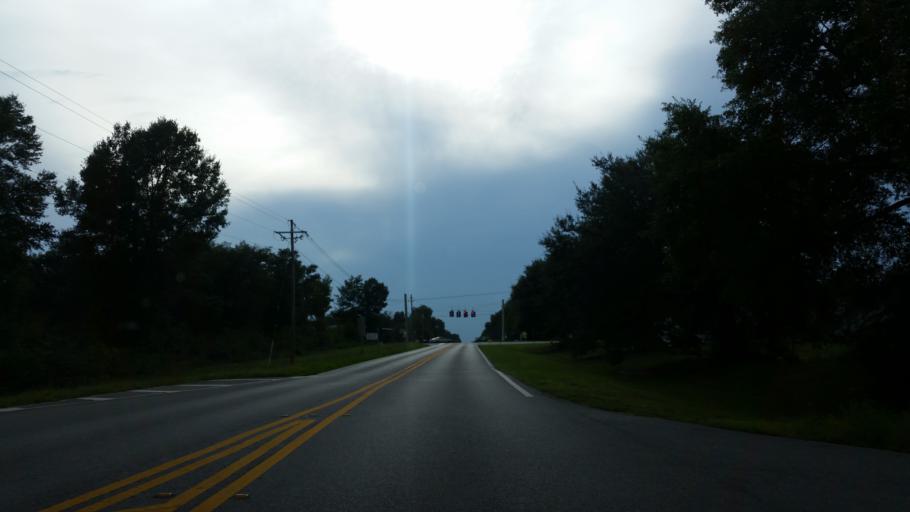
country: US
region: Florida
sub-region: Santa Rosa County
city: Bagdad
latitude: 30.5740
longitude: -87.0959
